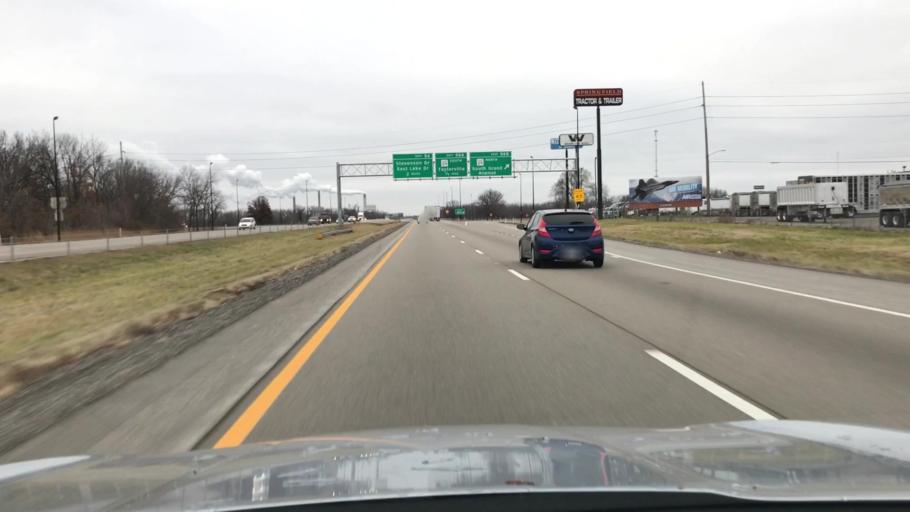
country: US
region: Illinois
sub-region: Sangamon County
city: Grandview
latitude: 39.7912
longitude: -89.5982
